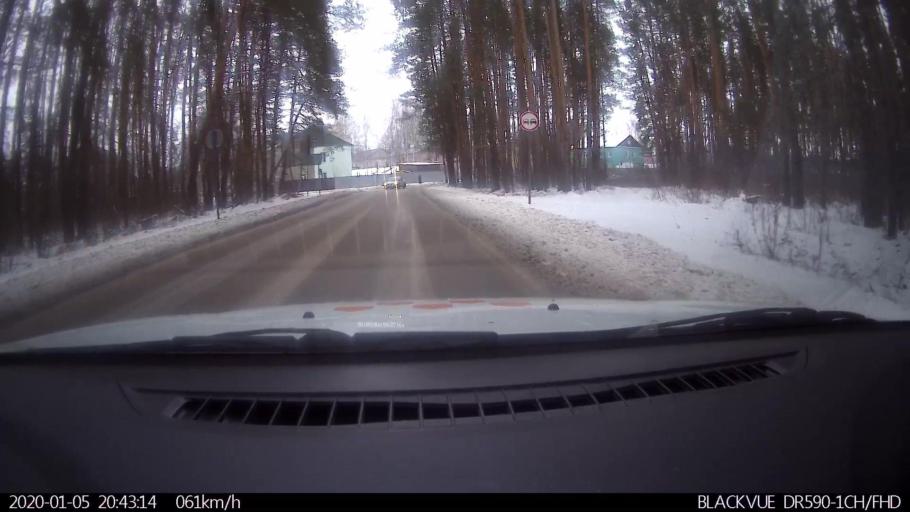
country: RU
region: Nizjnij Novgorod
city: Lukino
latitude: 56.3915
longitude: 43.7389
